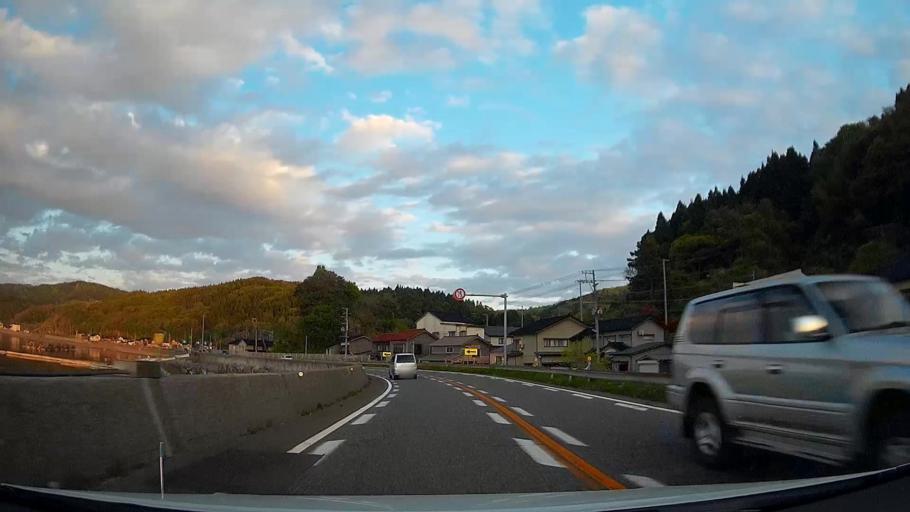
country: JP
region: Niigata
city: Itoigawa
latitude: 37.1150
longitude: 138.0138
